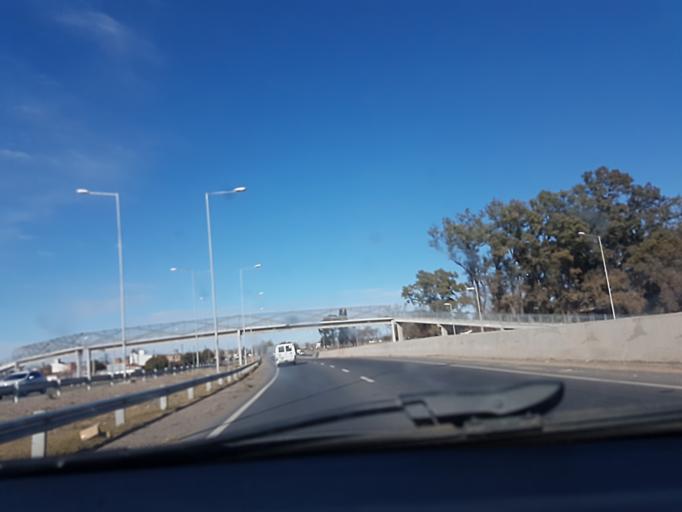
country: AR
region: Cordoba
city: La Calera
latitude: -31.3960
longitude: -64.2672
